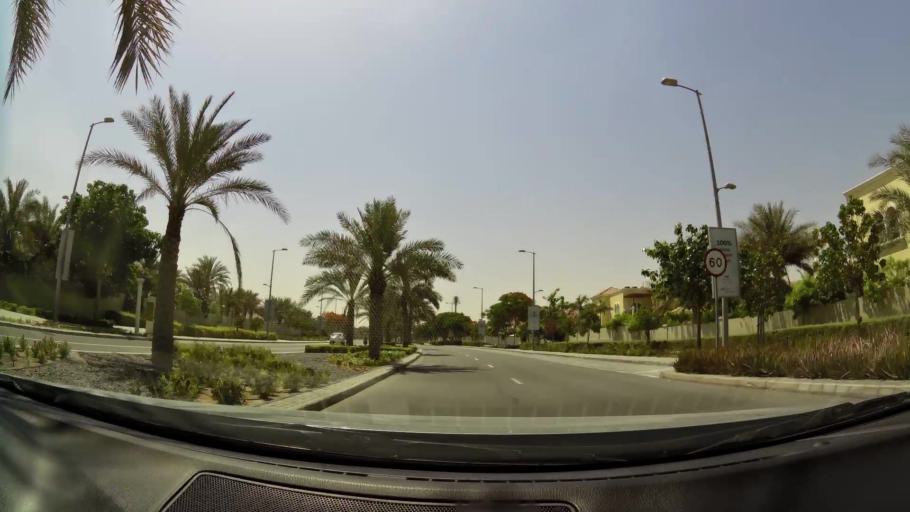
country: AE
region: Dubai
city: Dubai
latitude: 25.0520
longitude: 55.1480
